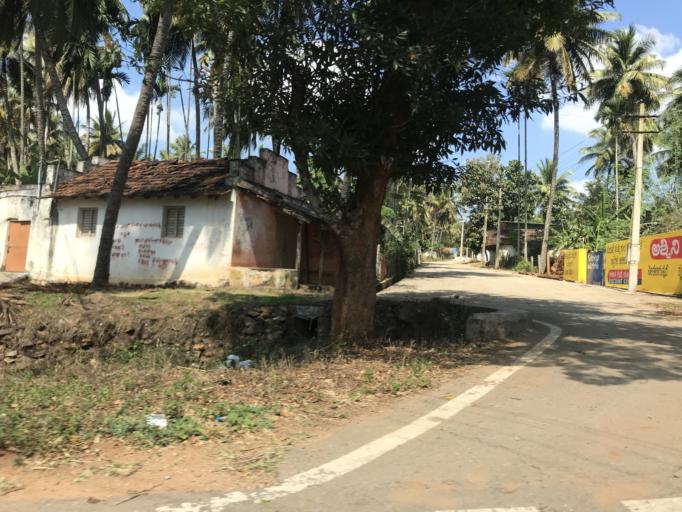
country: IN
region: Karnataka
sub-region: Mysore
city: Heggadadevankote
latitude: 12.1158
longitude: 76.3129
